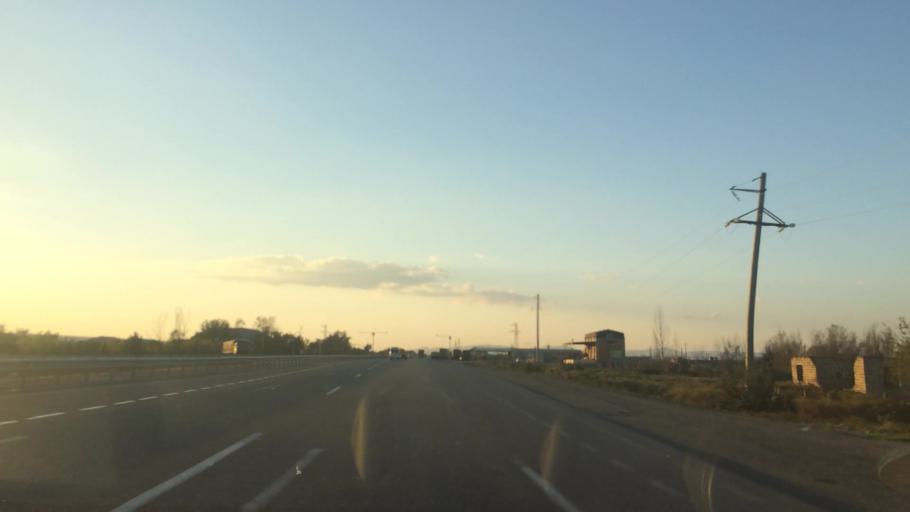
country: AZ
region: Haciqabul
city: Haciqabul
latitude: 40.0086
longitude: 49.1548
